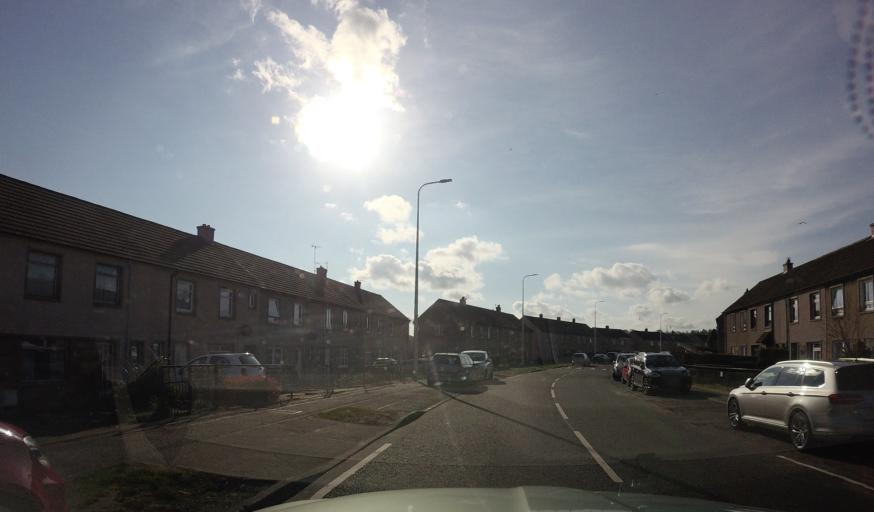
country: GB
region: Scotland
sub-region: Midlothian
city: Penicuik
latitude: 55.8354
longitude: -3.2115
